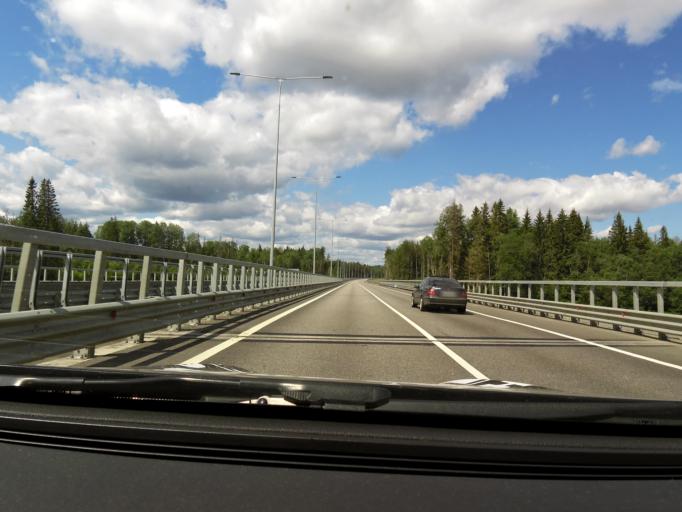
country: RU
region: Tverskaya
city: Vydropuzhsk
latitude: 57.2803
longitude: 34.8136
